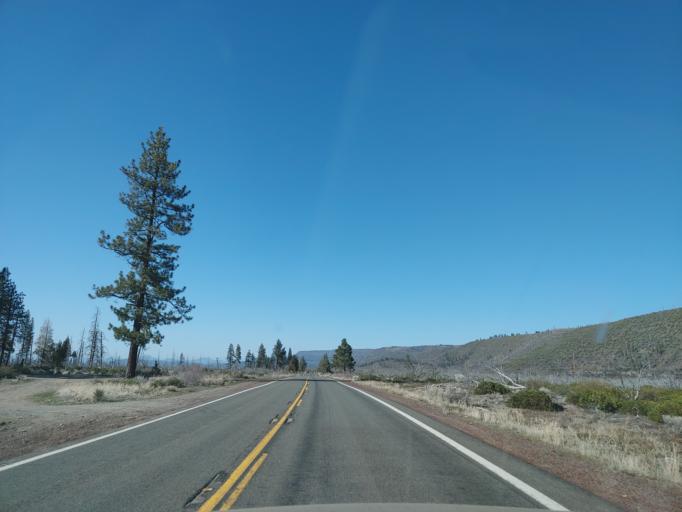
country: US
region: California
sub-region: Shasta County
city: Burney
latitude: 40.6957
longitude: -121.4181
